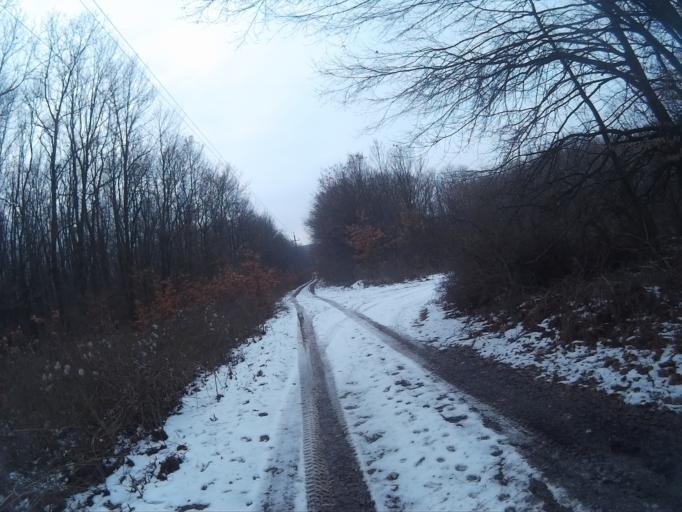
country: HU
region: Komarom-Esztergom
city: Nyergesujfalu
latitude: 47.7043
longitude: 18.5506
